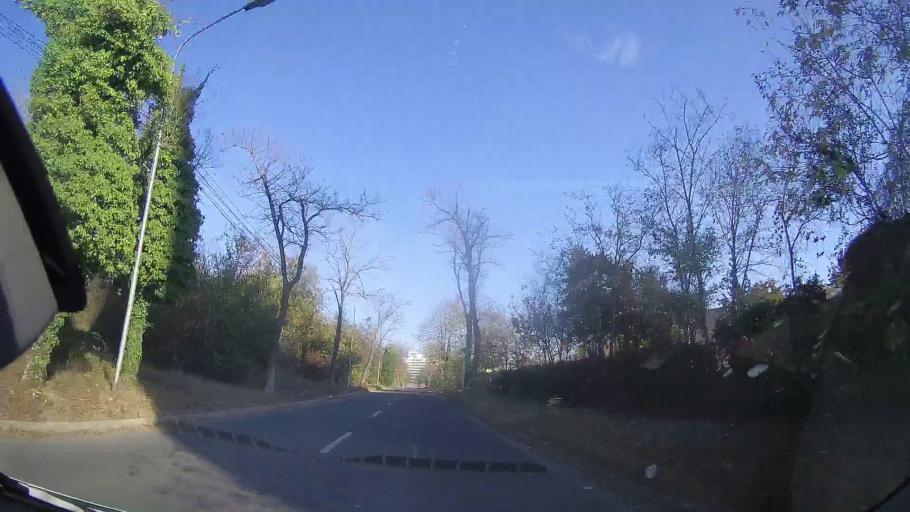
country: RO
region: Constanta
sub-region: Municipiul Mangalia
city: Mangalia
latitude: 43.8476
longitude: 28.5964
